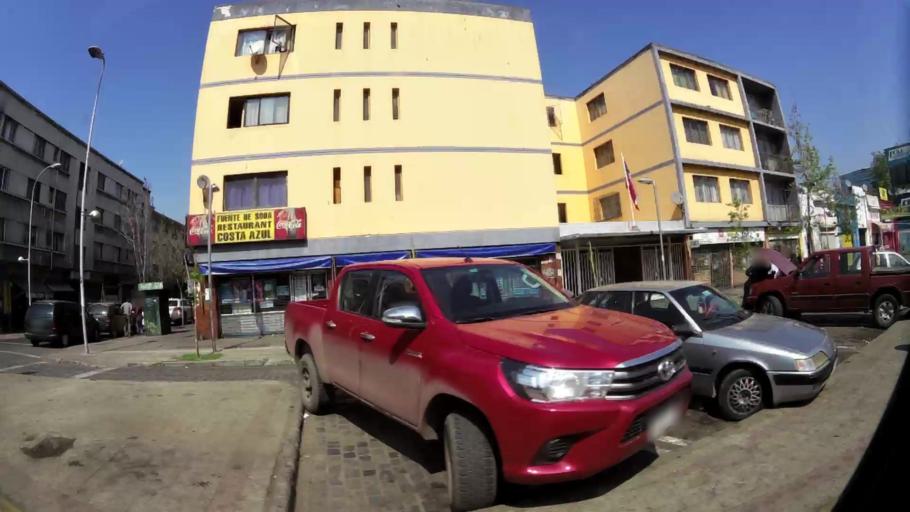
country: CL
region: Santiago Metropolitan
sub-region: Provincia de Santiago
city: Santiago
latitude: -33.4541
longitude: -70.6487
